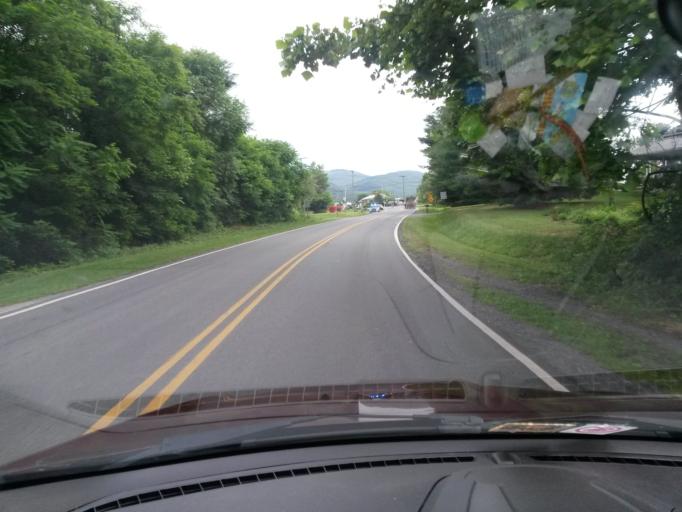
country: US
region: Virginia
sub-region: City of Covington
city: Fairlawn
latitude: 37.7705
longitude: -79.9697
